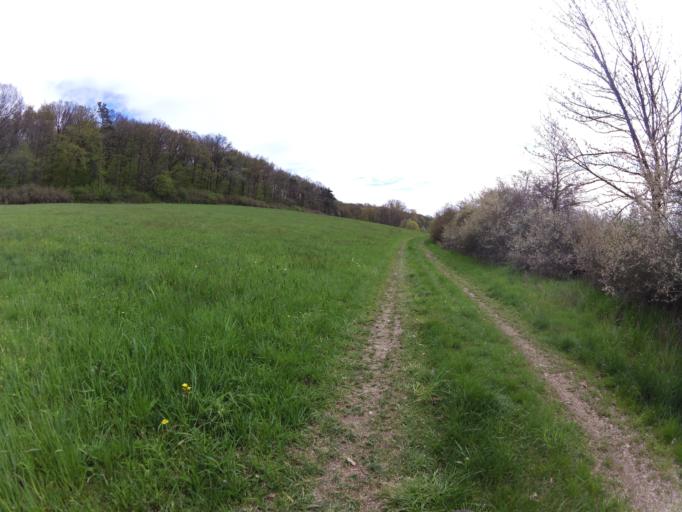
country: DE
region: Bavaria
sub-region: Regierungsbezirk Unterfranken
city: Prosselsheim
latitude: 49.8590
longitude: 10.1449
